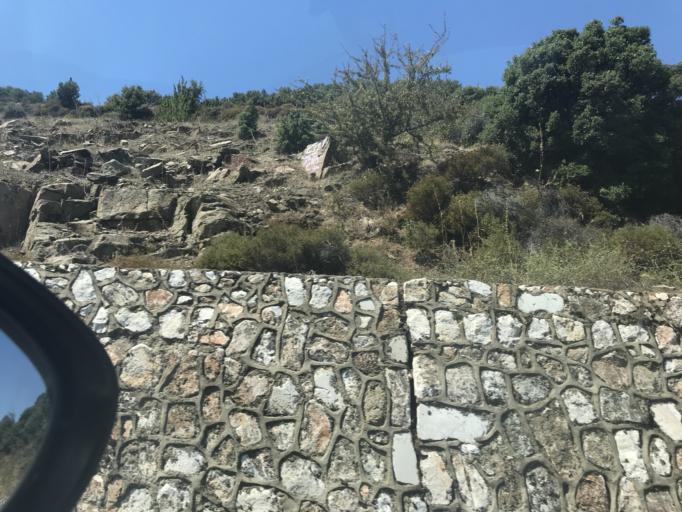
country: TR
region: Aydin
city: Akcaova
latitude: 37.5075
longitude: 28.1019
